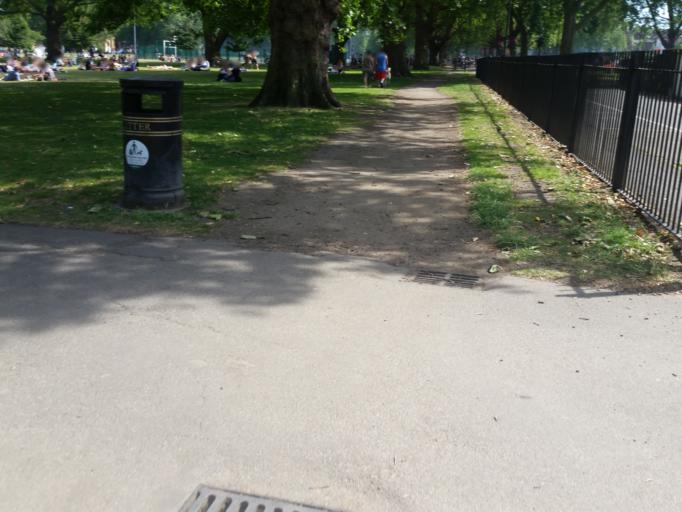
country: GB
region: England
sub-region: Greater London
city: Bethnal Green
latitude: 51.5410
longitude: -0.0615
